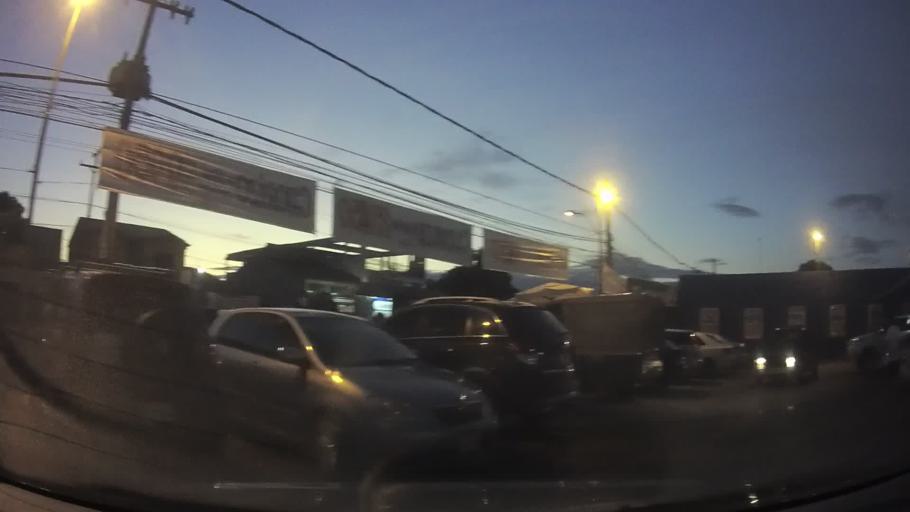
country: PY
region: Central
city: Itaugua
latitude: -25.3923
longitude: -57.3542
